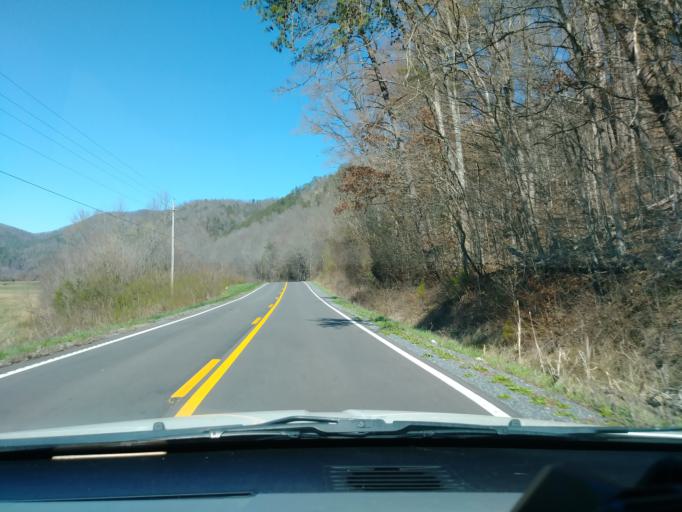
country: US
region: Tennessee
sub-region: Cocke County
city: Newport
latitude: 35.9191
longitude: -82.9901
